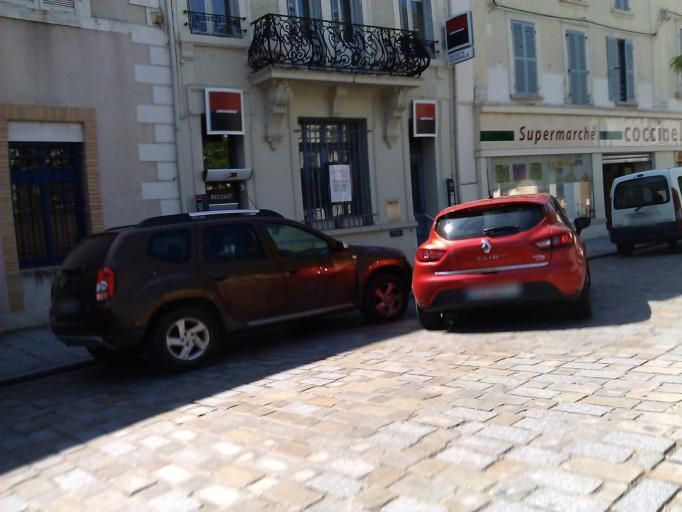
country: FR
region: Centre
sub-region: Departement de l'Indre
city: Argenton-sur-Creuse
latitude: 46.5886
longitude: 1.5192
